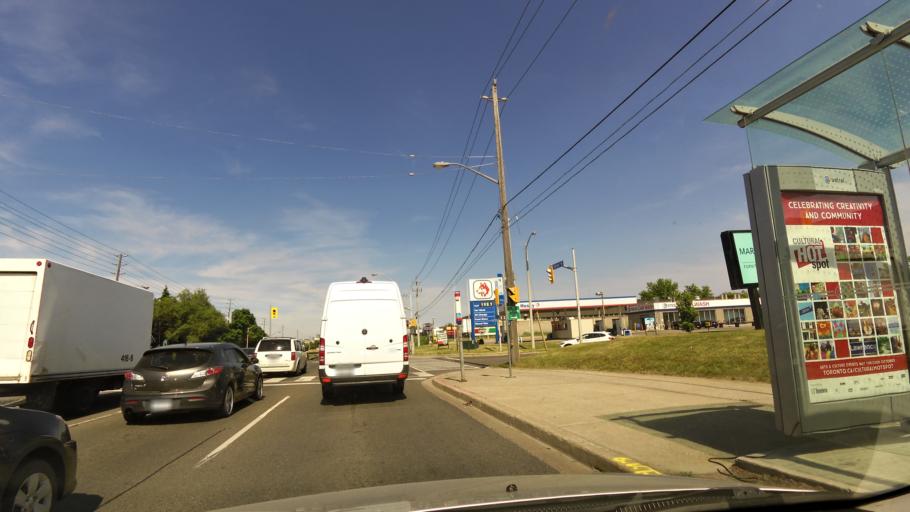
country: CA
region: Ontario
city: Concord
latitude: 43.7830
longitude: -79.4876
